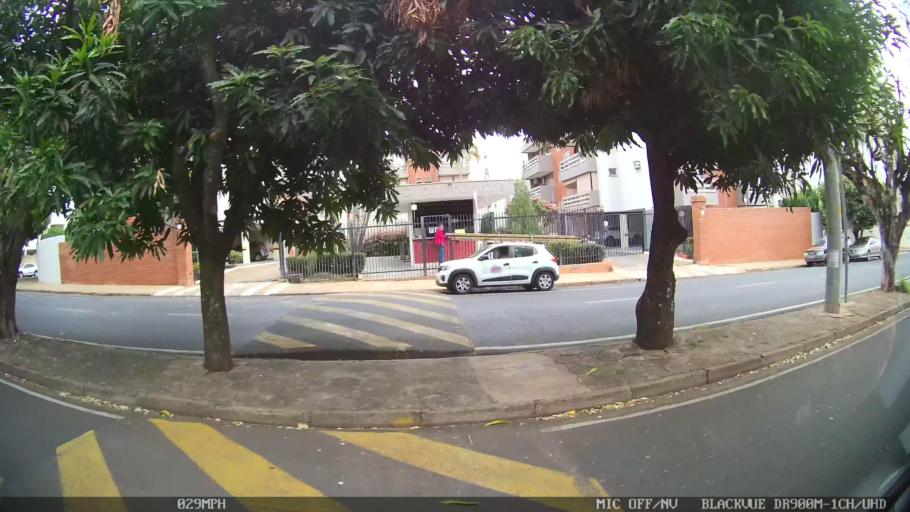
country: BR
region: Sao Paulo
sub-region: Sao Jose Do Rio Preto
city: Sao Jose do Rio Preto
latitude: -20.8326
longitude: -49.3877
